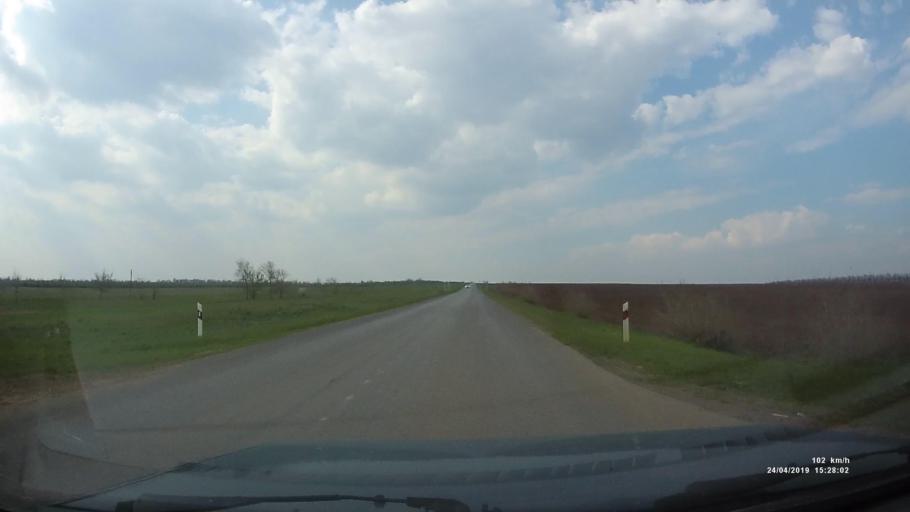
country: RU
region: Rostov
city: Remontnoye
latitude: 46.5733
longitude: 43.0213
